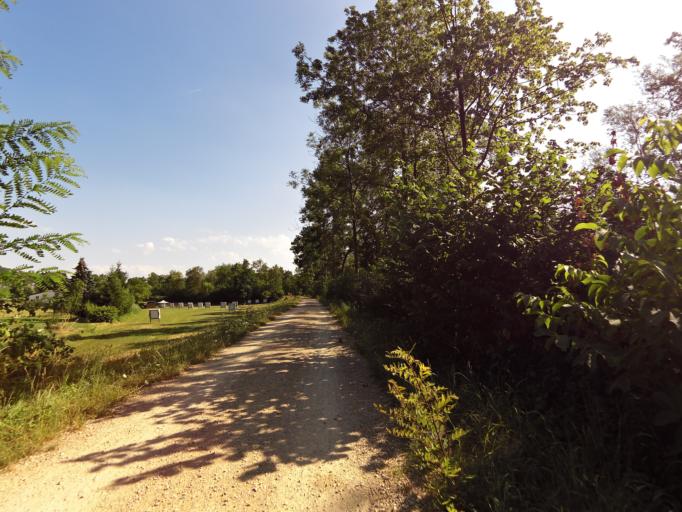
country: CH
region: Aargau
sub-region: Bezirk Brugg
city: Schinznach Bad
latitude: 47.4336
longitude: 8.1638
